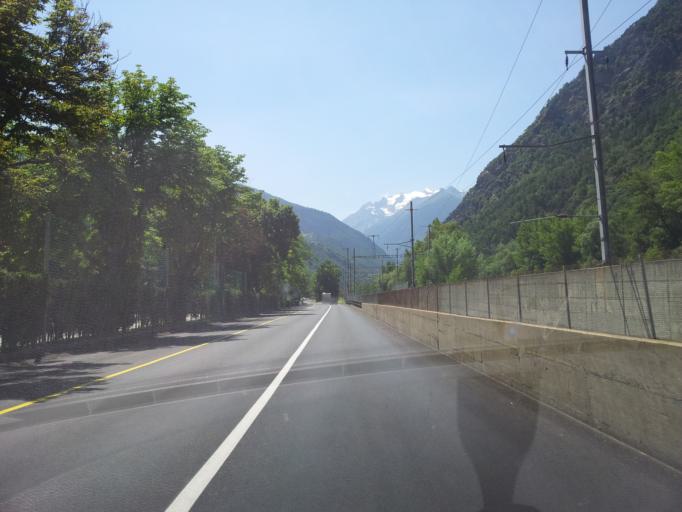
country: CH
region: Valais
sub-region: Visp District
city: Visp
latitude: 46.2907
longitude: 7.8796
